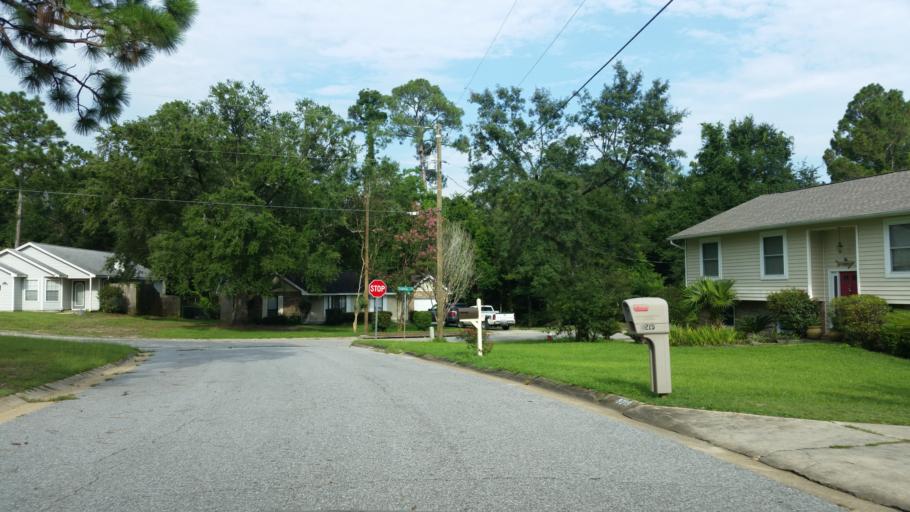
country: US
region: Florida
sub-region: Escambia County
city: Ferry Pass
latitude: 30.5092
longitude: -87.1752
